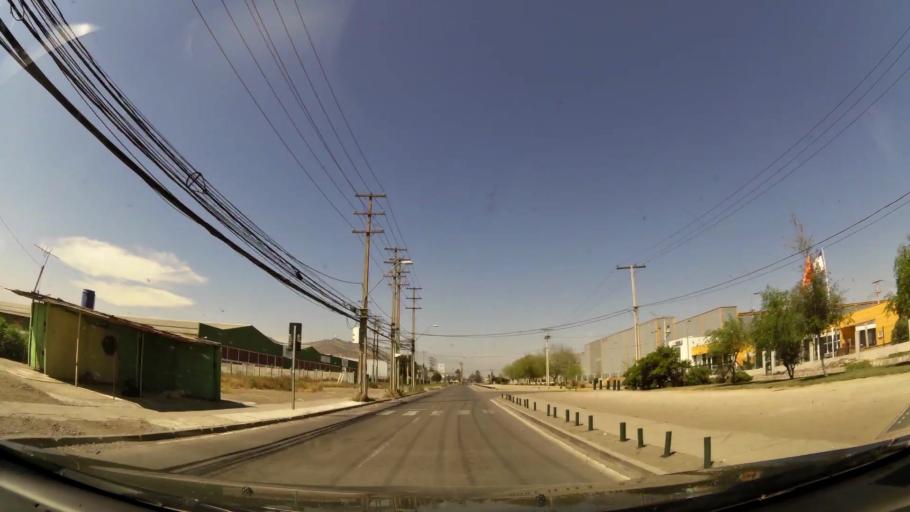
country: CL
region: Santiago Metropolitan
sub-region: Provincia de Santiago
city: Lo Prado
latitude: -33.3824
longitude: -70.7669
